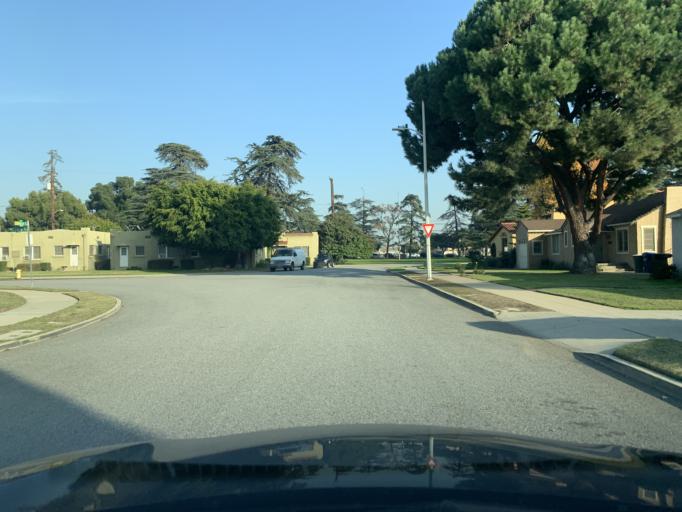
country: US
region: California
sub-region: Los Angeles County
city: Covina
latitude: 34.0872
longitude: -117.8966
